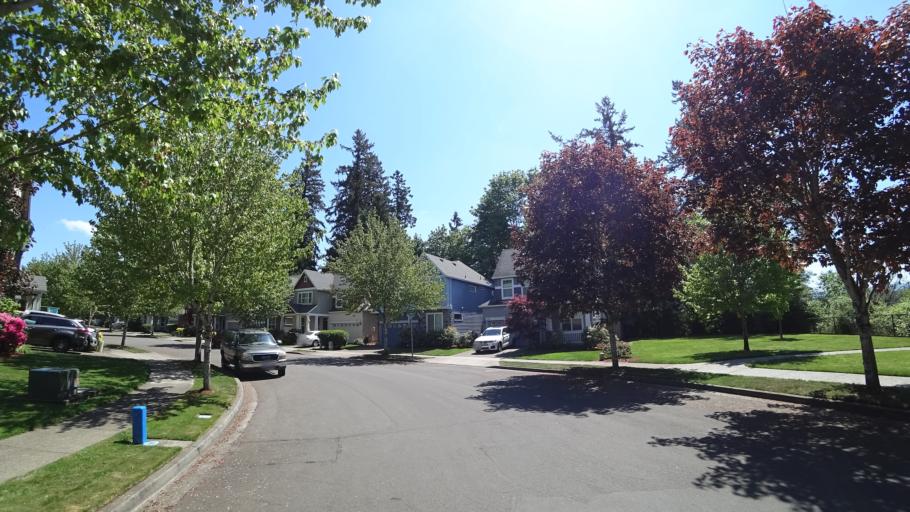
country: US
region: Oregon
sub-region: Washington County
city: Hillsboro
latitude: 45.5075
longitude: -122.9761
